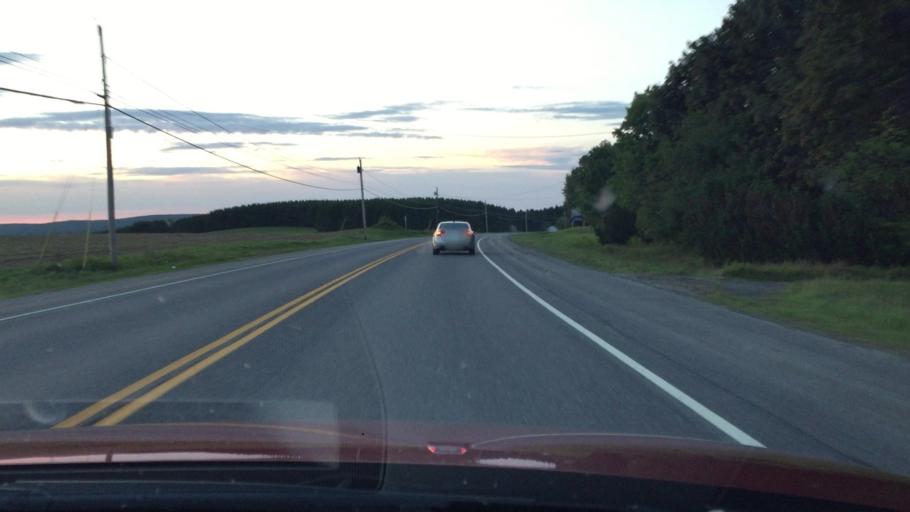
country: US
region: Maine
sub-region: Aroostook County
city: Easton
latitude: 46.4643
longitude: -67.8661
